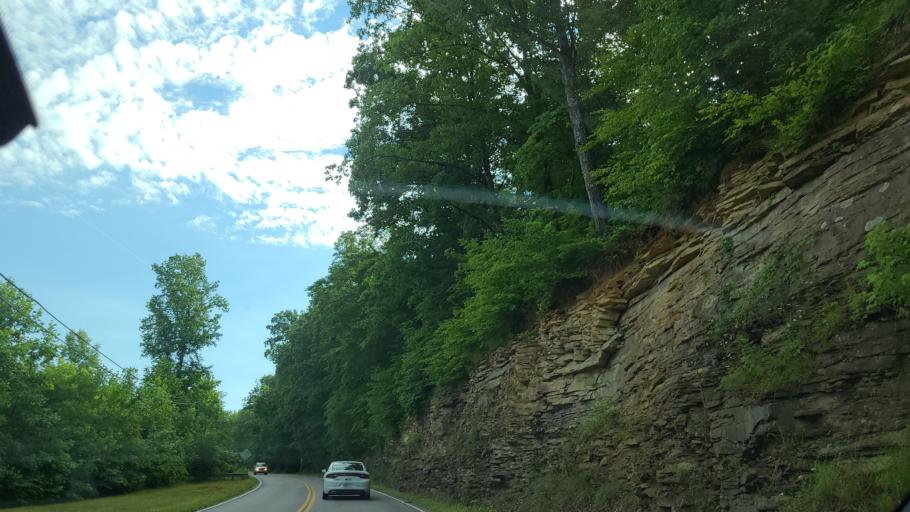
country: US
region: Kentucky
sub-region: Whitley County
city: Williamsburg
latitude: 36.7426
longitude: -84.0648
